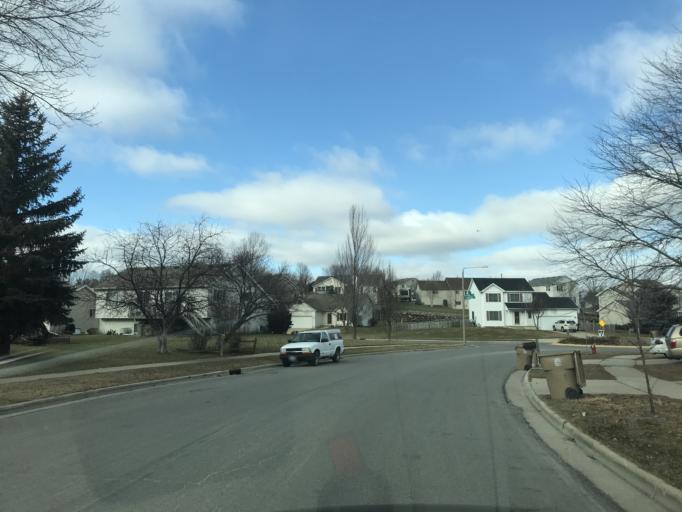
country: US
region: Wisconsin
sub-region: Dane County
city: Monona
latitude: 43.1192
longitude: -89.2911
